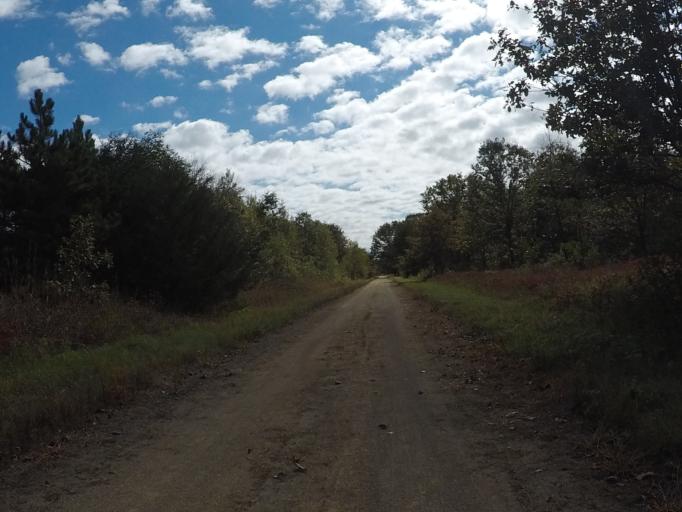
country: US
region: Wisconsin
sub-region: Sauk County
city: Spring Green
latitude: 43.1901
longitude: -90.2205
